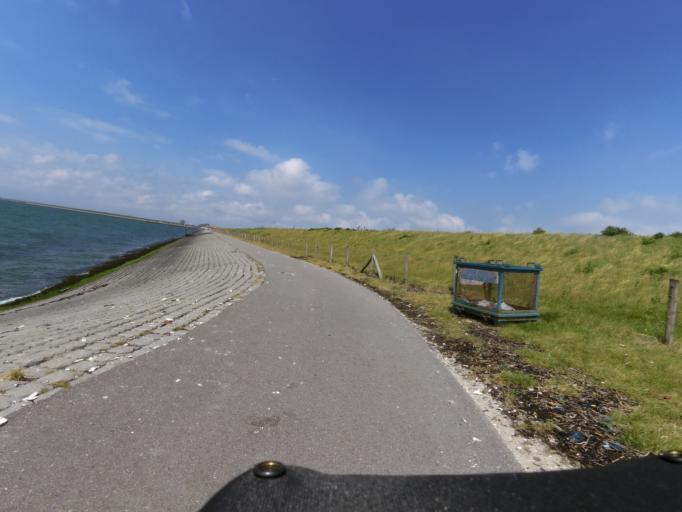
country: NL
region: Zeeland
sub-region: Schouwen-Duiveland
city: Scharendijke
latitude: 51.6745
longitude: 3.8653
